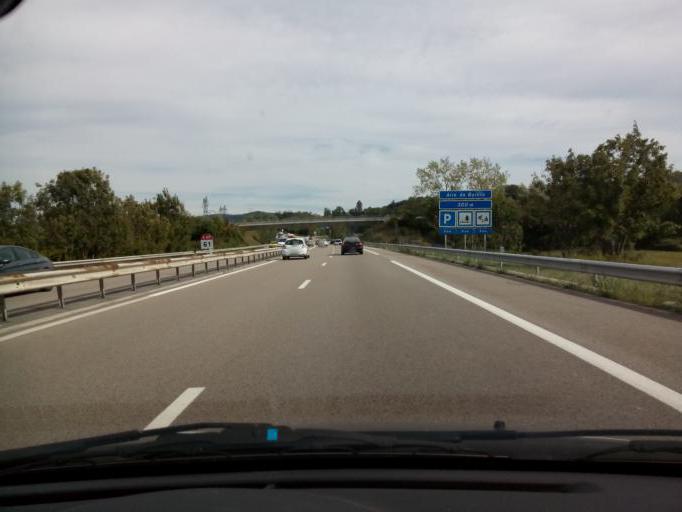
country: FR
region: Rhone-Alpes
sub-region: Departement de l'Isere
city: Chabons
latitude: 45.4279
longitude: 5.4298
